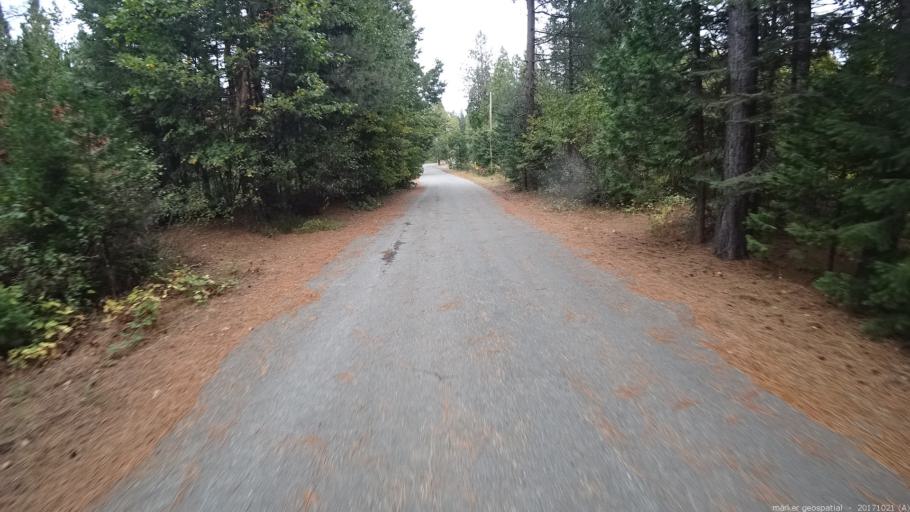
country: US
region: California
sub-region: Shasta County
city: Burney
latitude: 40.8646
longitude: -121.9085
